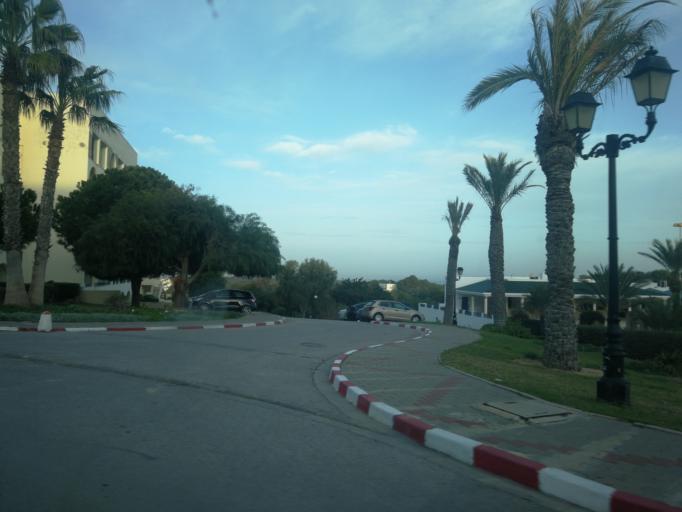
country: TN
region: Tunis
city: Al Marsa
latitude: 36.9058
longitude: 10.3130
